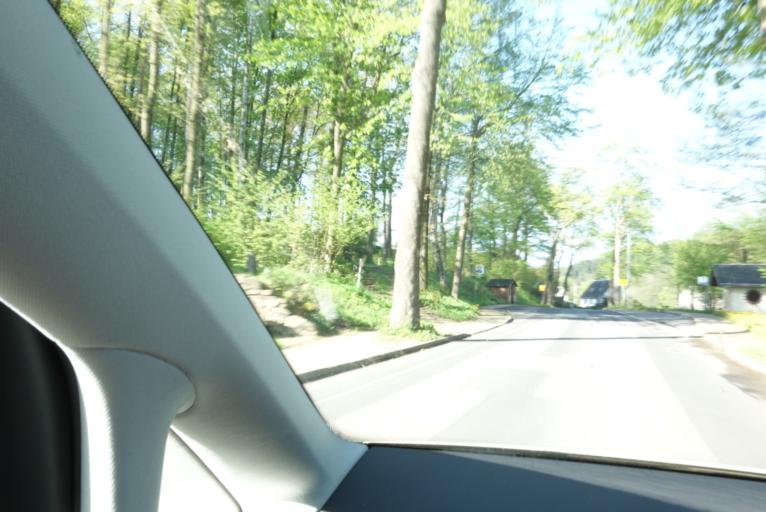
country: DE
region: Saxony
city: Pfaffroda
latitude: 50.6948
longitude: 13.3534
